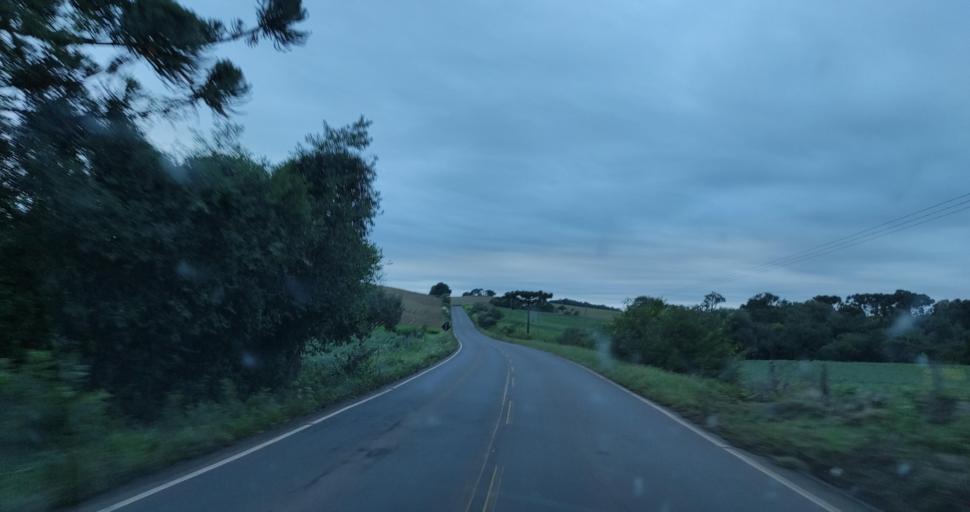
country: BR
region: Santa Catarina
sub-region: Xanxere
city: Xanxere
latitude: -26.7225
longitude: -52.4103
